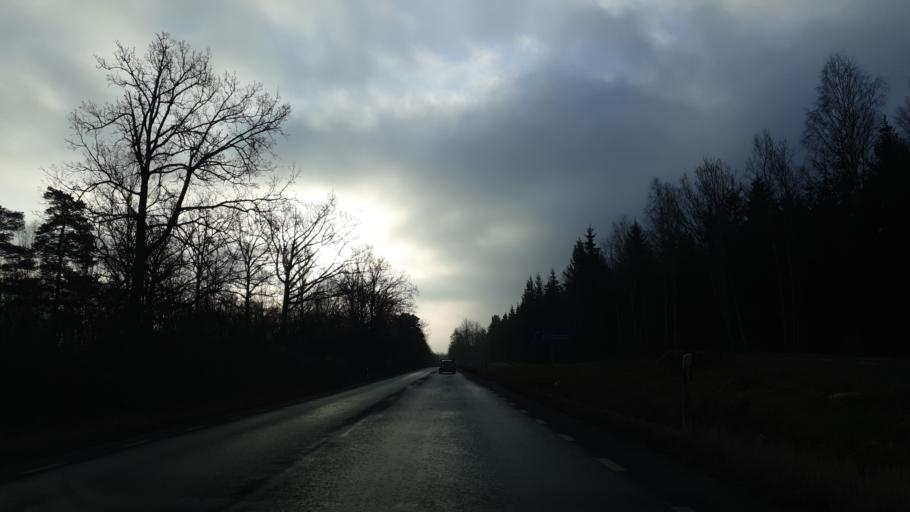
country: SE
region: Blekinge
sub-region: Karlshamns Kommun
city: Morrum
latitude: 56.1417
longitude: 14.6700
